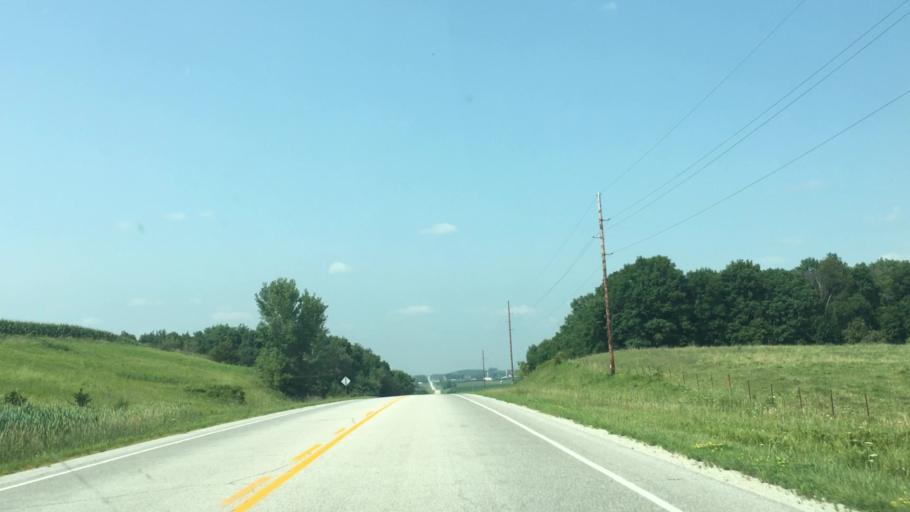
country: US
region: Minnesota
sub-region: Fillmore County
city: Harmony
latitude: 43.5853
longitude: -91.9298
